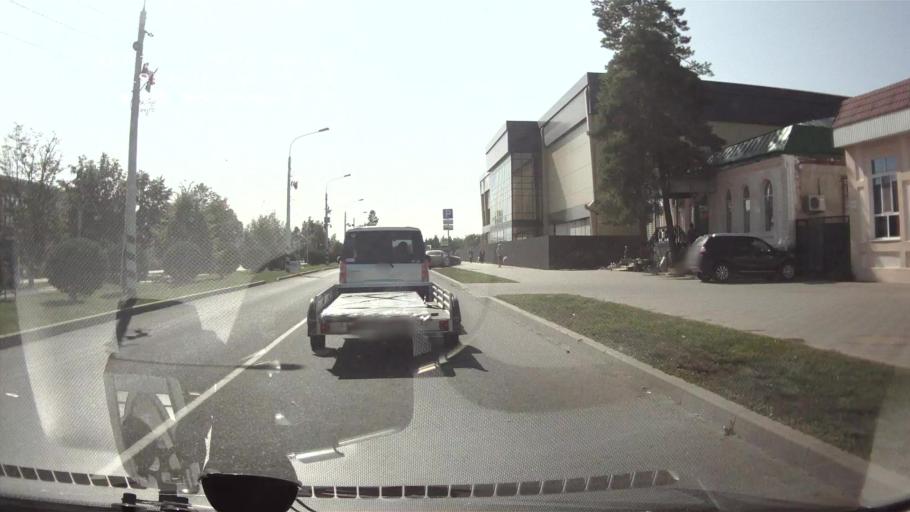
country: RU
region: Krasnodarskiy
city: Novopokrovskaya
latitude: 45.9521
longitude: 40.7084
